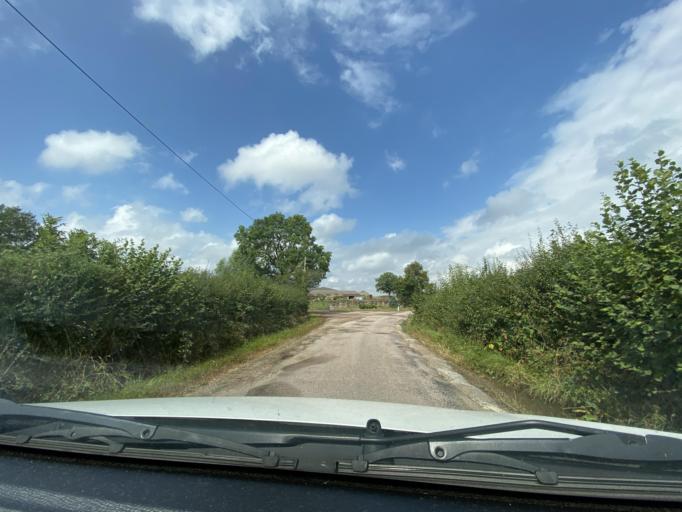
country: FR
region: Bourgogne
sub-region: Departement de la Cote-d'Or
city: Saulieu
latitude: 47.2868
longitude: 4.2379
